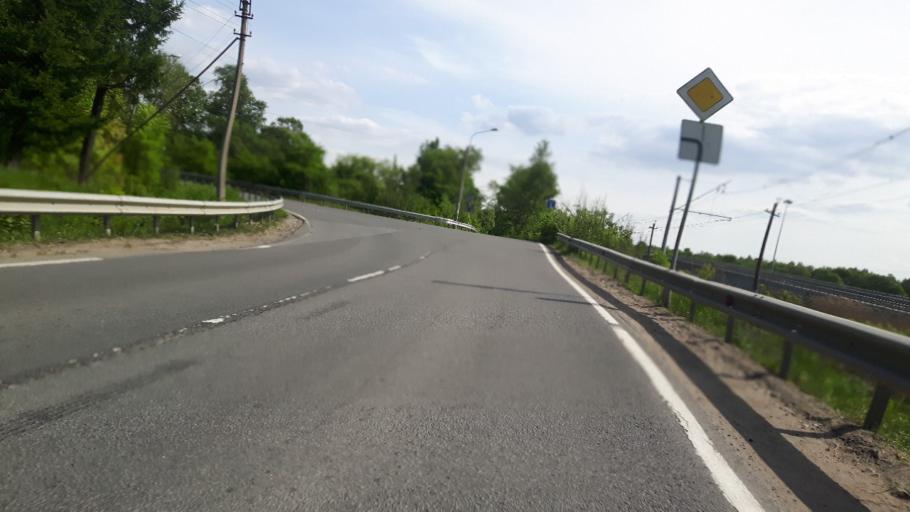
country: RU
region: Leningrad
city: Gorskaya
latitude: 60.0373
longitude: 29.9783
